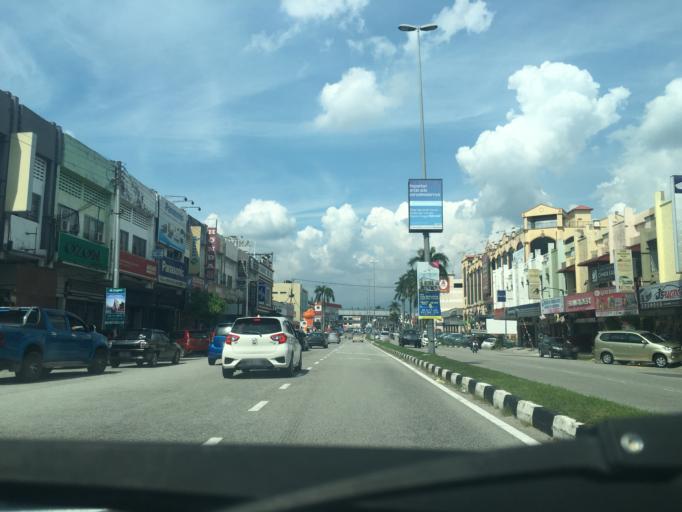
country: MY
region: Perak
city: Ipoh
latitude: 4.5847
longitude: 101.0884
